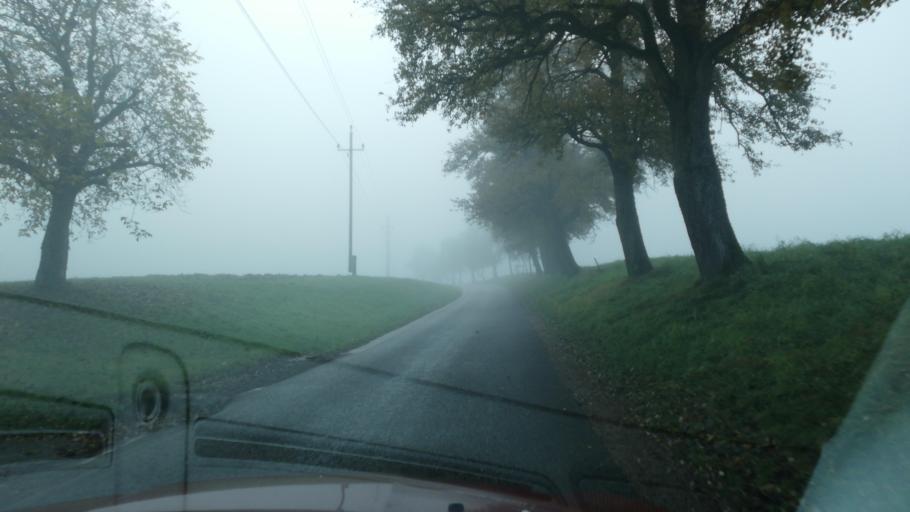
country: AT
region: Upper Austria
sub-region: Politischer Bezirk Grieskirchen
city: Bad Schallerbach
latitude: 48.2118
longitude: 13.8865
